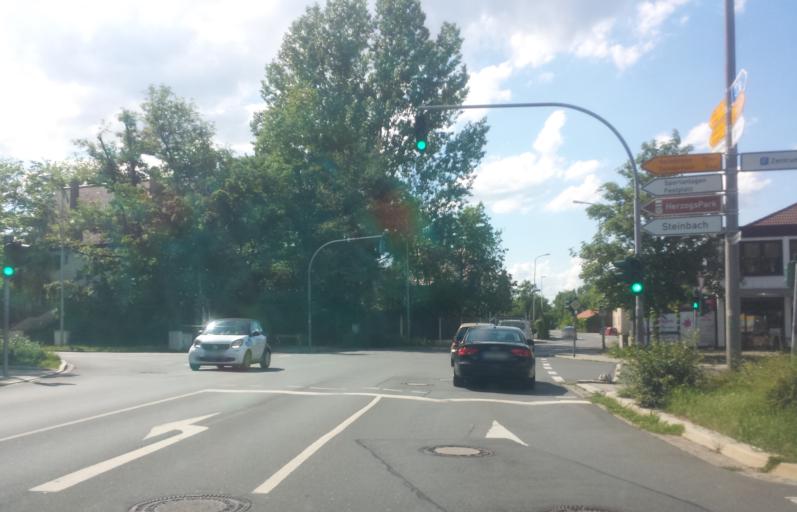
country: DE
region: Bavaria
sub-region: Regierungsbezirk Mittelfranken
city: Herzogenaurach
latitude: 49.5677
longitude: 10.8788
